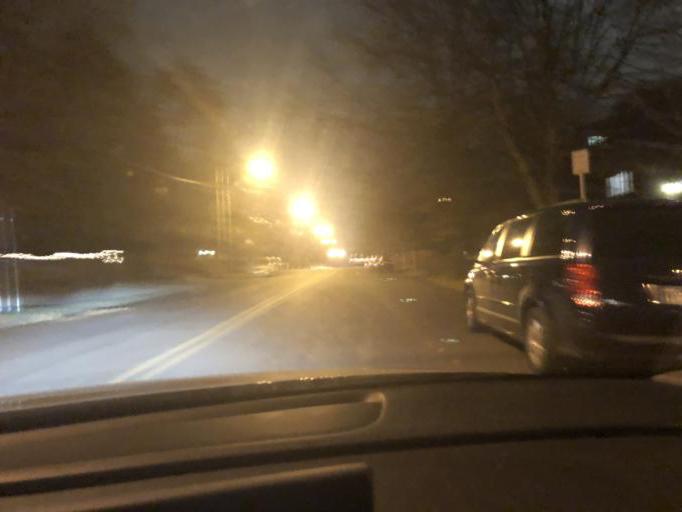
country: US
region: New Jersey
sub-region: Hudson County
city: East Newark
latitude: 40.7678
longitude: -74.1741
